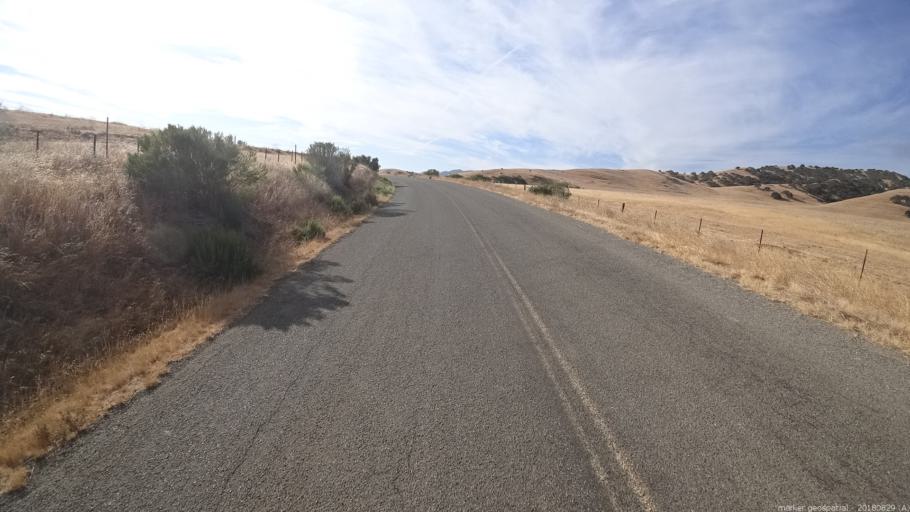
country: US
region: California
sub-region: Monterey County
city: King City
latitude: 36.0302
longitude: -120.9604
